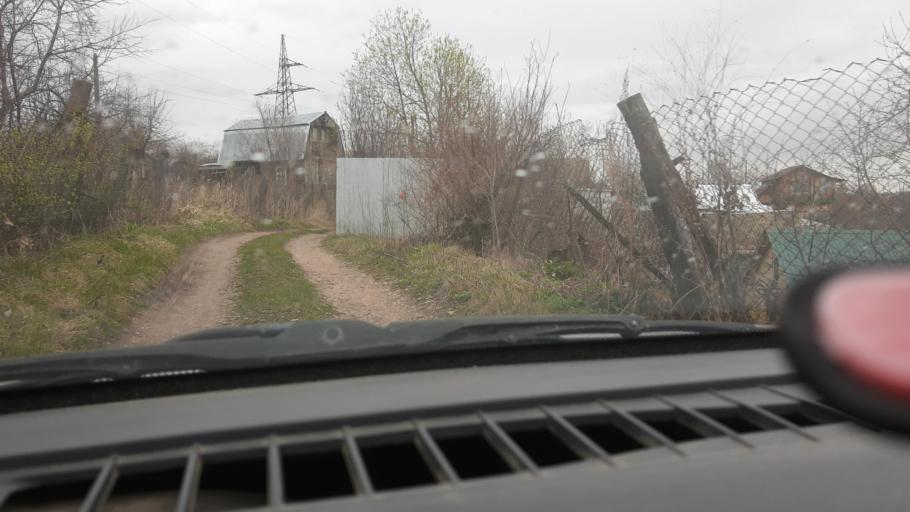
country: RU
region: Bashkortostan
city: Mikhaylovka
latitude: 54.9199
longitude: 55.8869
